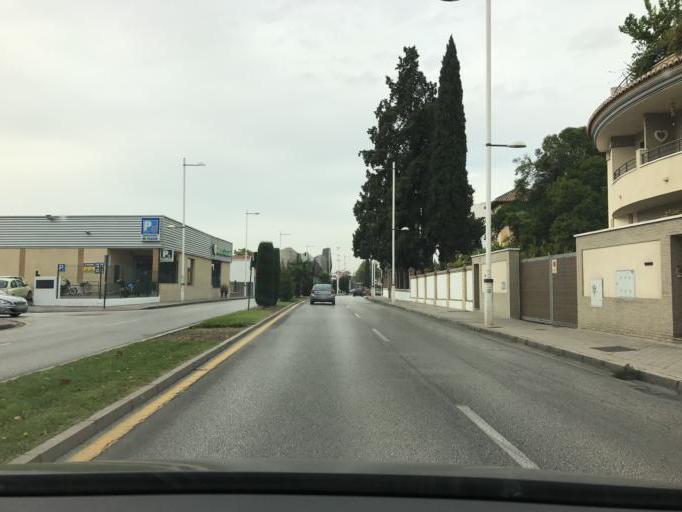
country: ES
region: Andalusia
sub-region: Provincia de Granada
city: Armilla
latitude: 37.1599
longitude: -3.6056
